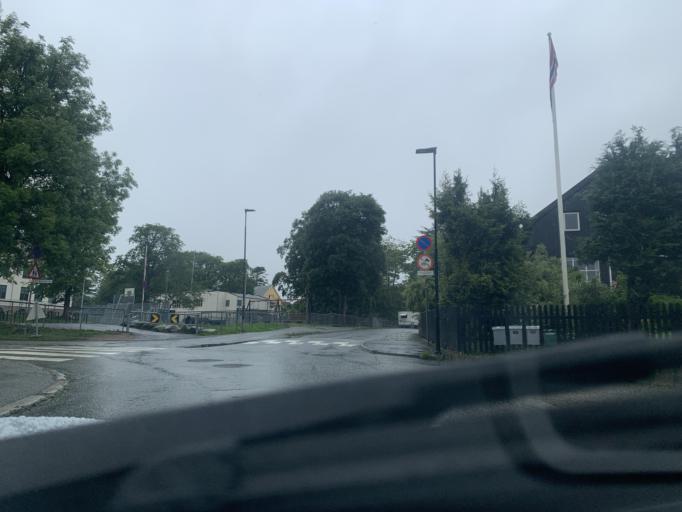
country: NO
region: Rogaland
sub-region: Time
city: Bryne
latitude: 58.7321
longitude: 5.6462
